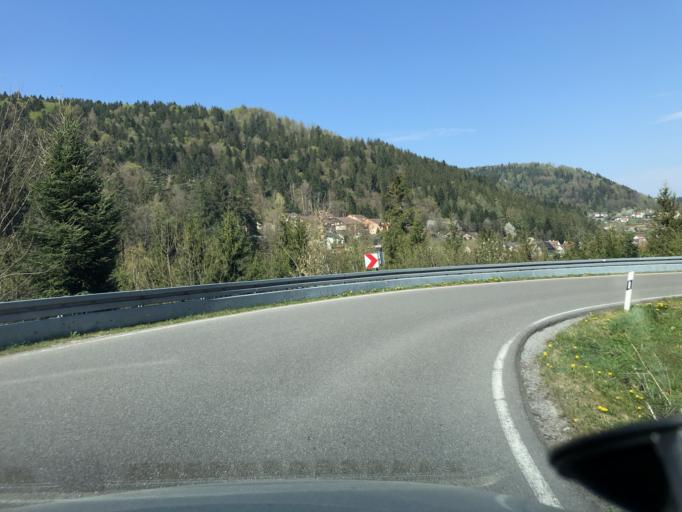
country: DE
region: Baden-Wuerttemberg
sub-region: Karlsruhe Region
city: Unterreichenbach
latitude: 48.8180
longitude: 8.7175
